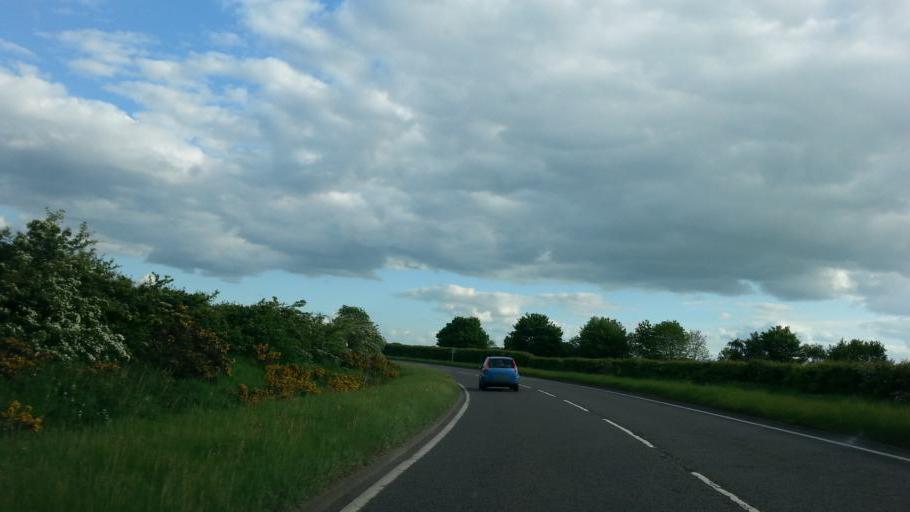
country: GB
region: England
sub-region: Nottinghamshire
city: South Collingham
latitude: 53.1059
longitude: -0.7783
